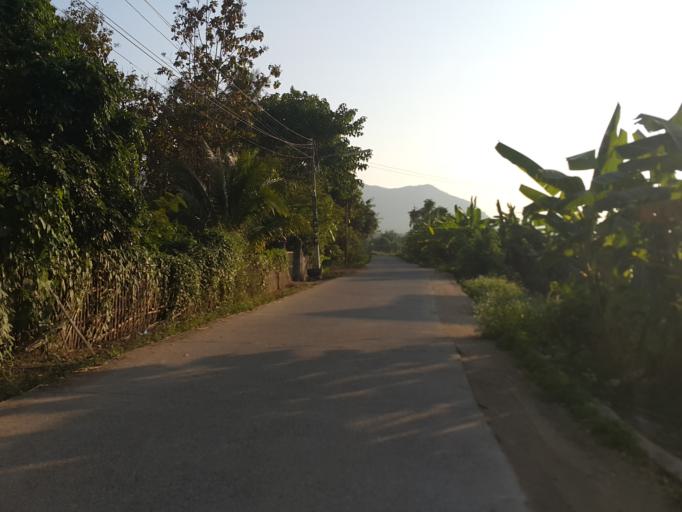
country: TH
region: Chiang Mai
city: Mae On
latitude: 18.7597
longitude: 99.2572
